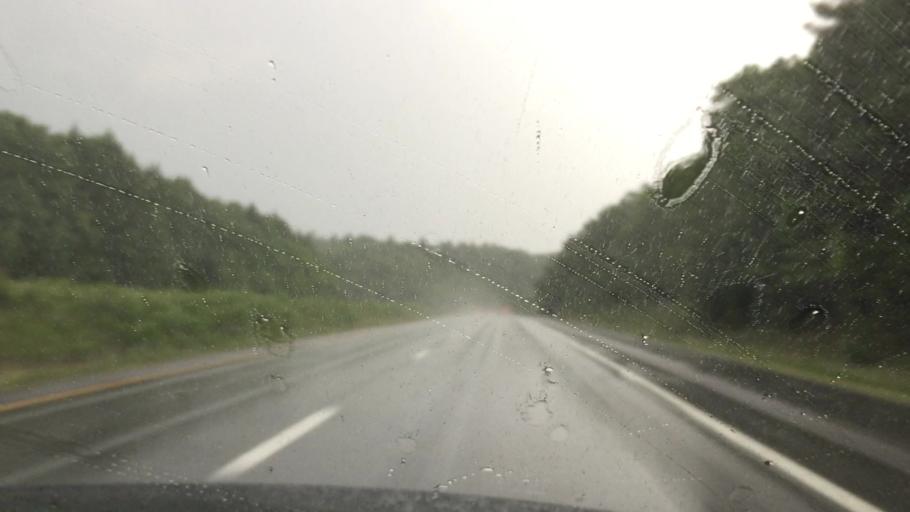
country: US
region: New Hampshire
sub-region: Merrimack County
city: Hill
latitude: 43.5763
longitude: -71.6243
